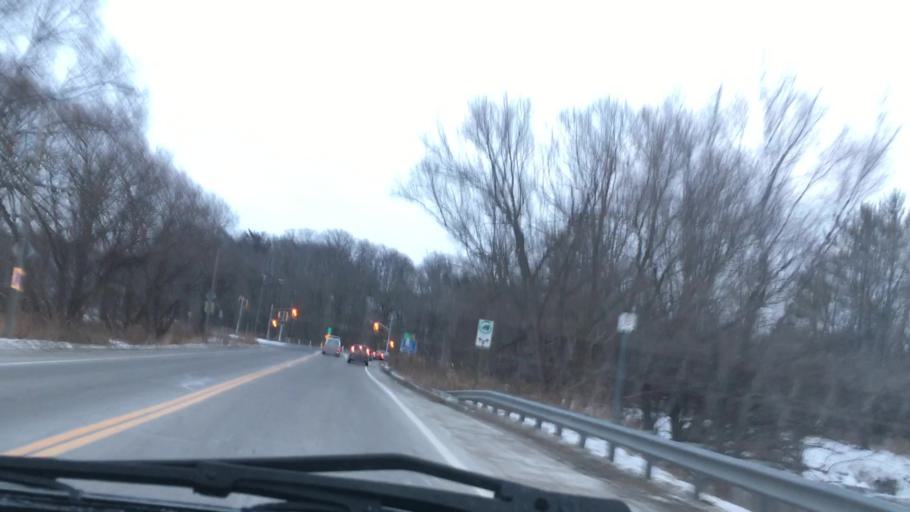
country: CA
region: Ontario
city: Ancaster
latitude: 43.2684
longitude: -79.9366
